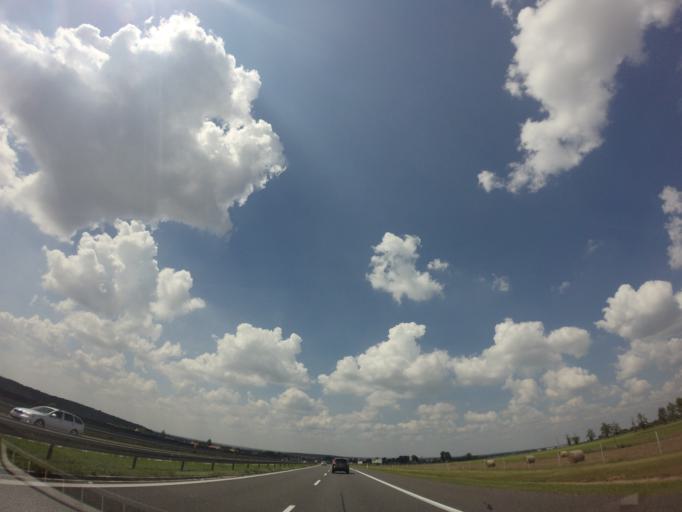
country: PL
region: Opole Voivodeship
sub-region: Powiat krapkowicki
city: Gogolin
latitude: 50.4833
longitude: 18.0474
